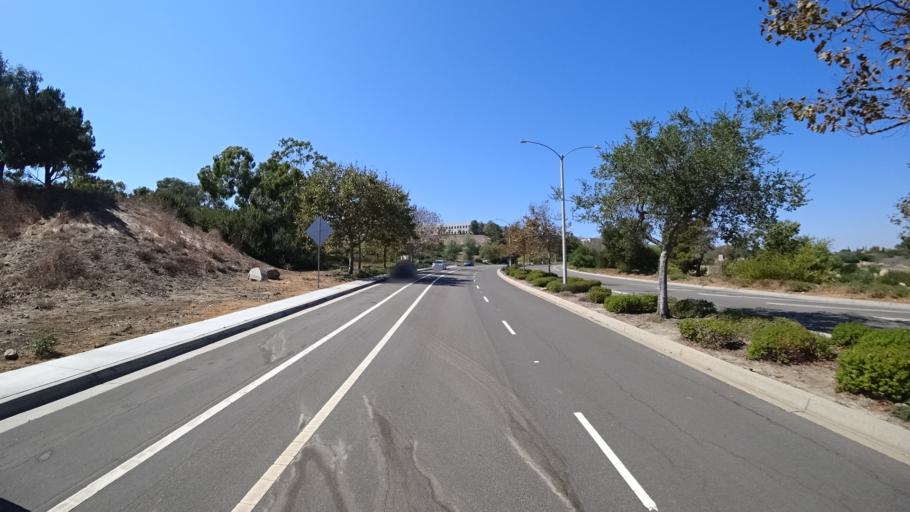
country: US
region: California
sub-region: Orange County
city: San Clemente
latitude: 33.4459
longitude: -117.5835
